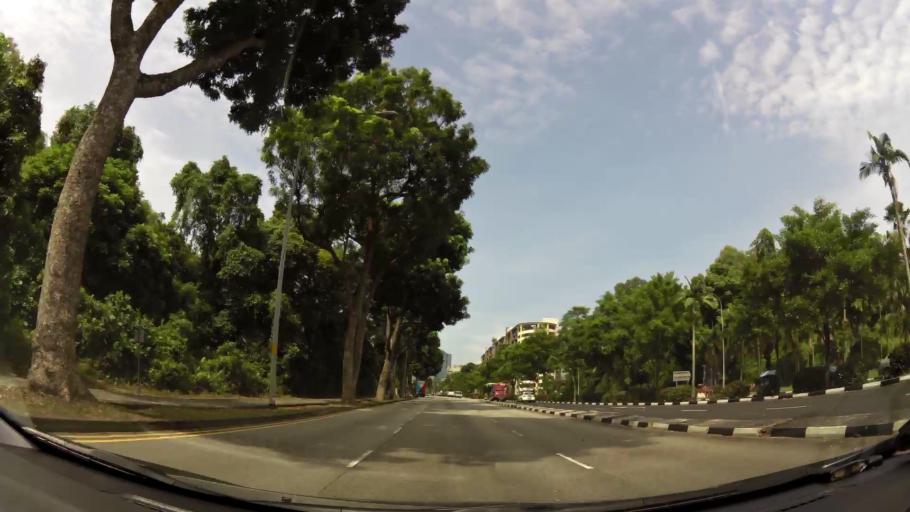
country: SG
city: Singapore
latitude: 1.3259
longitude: 103.7566
